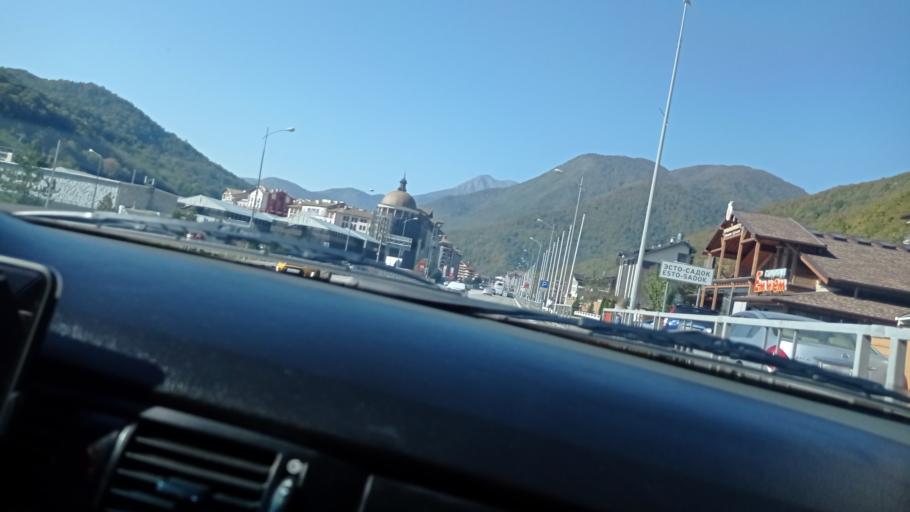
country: RU
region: Krasnodarskiy
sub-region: Sochi City
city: Krasnaya Polyana
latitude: 43.6819
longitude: 40.2736
